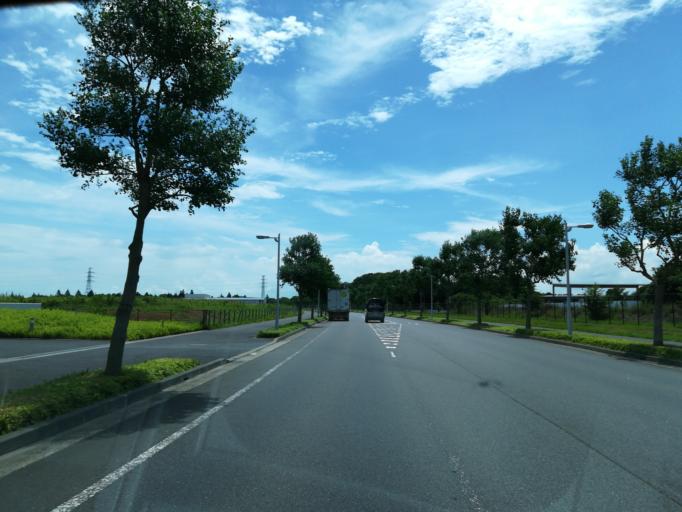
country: JP
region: Ibaraki
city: Naka
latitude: 36.0791
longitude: 140.0792
